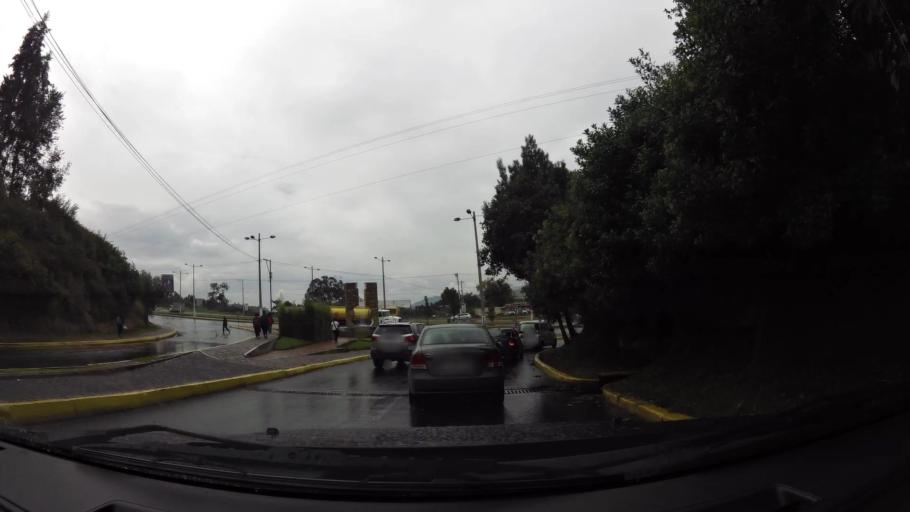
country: EC
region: Pichincha
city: Sangolqui
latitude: -0.2835
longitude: -78.4708
